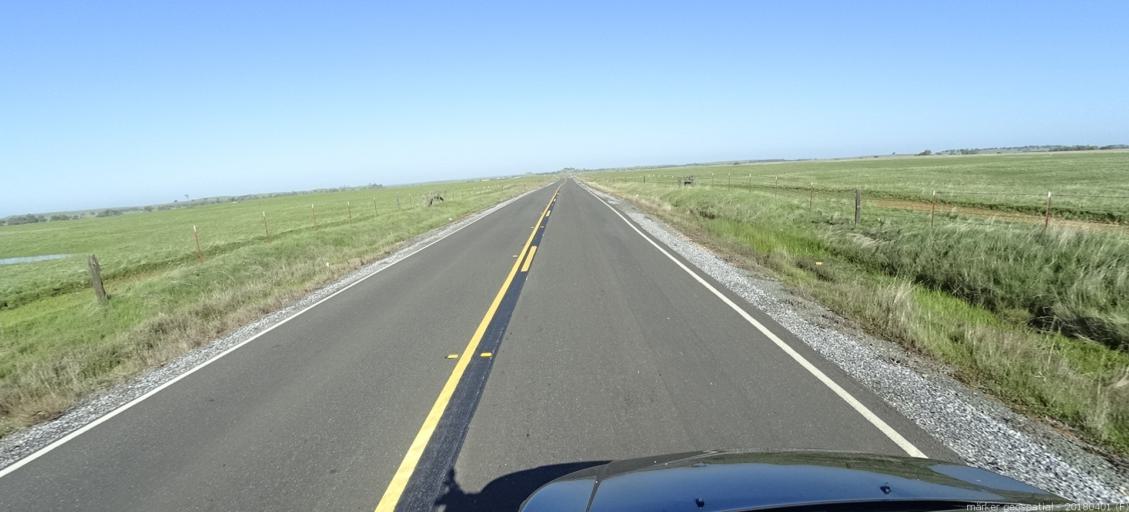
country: US
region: California
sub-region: Amador County
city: Ione
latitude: 38.4063
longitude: -121.0244
